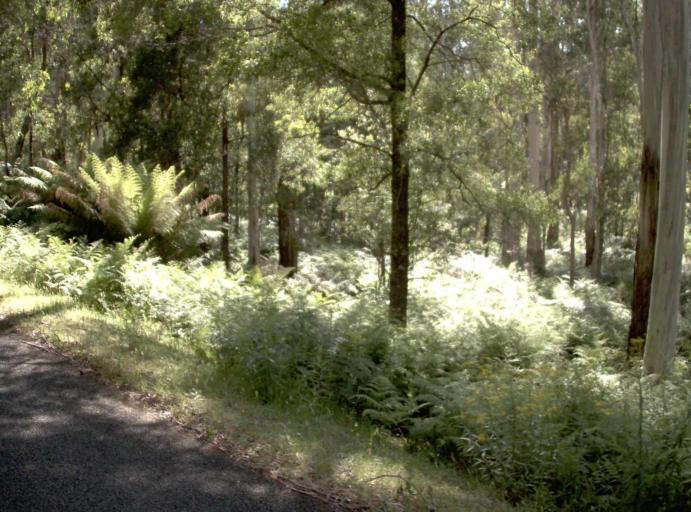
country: AU
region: New South Wales
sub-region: Bombala
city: Bombala
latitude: -37.3547
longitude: 148.6871
